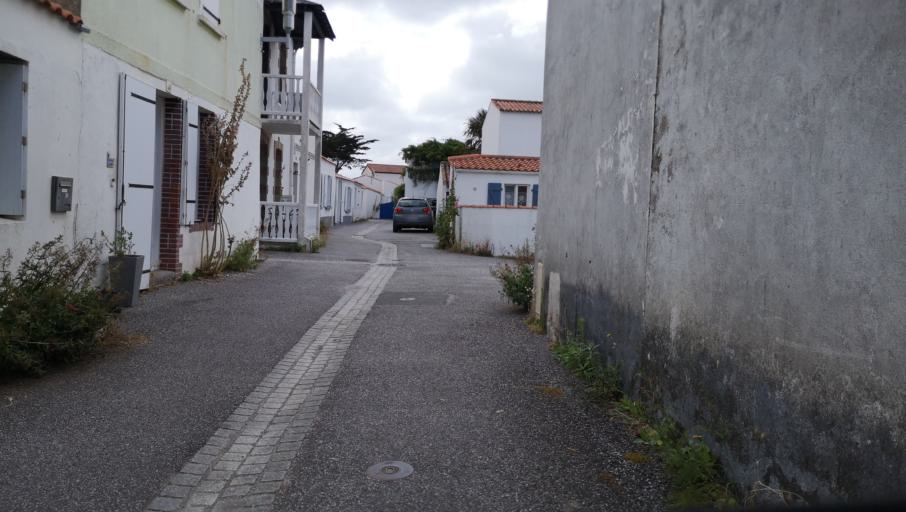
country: FR
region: Pays de la Loire
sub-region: Departement de la Vendee
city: Bretignolles-sur-Mer
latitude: 46.5949
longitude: -1.8325
